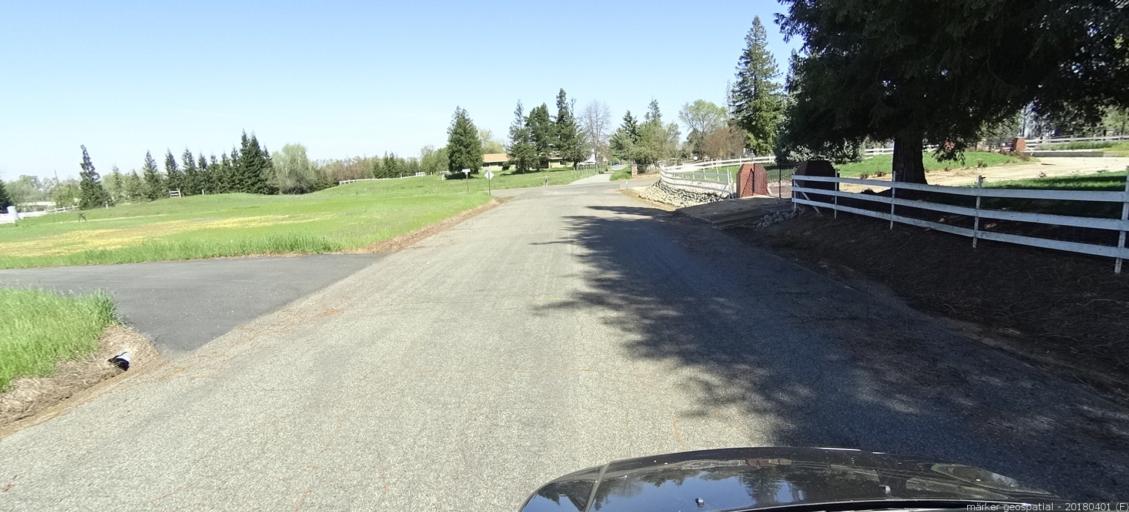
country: US
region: California
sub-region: Sacramento County
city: Wilton
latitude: 38.4167
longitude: -121.2216
